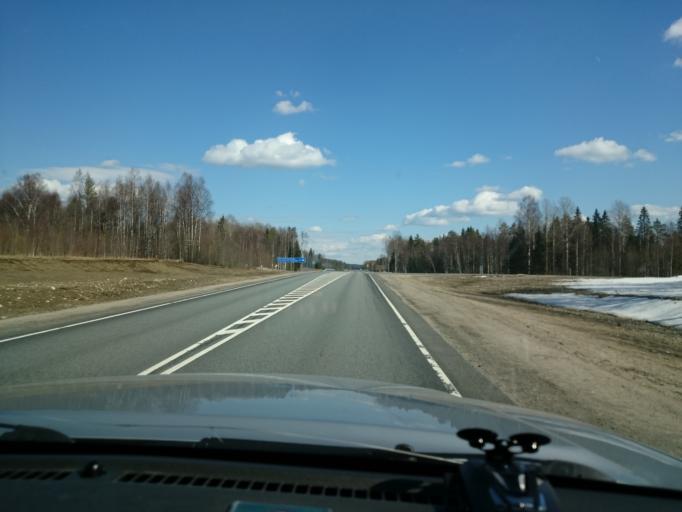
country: RU
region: Republic of Karelia
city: Pryazha
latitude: 61.5284
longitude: 33.5083
